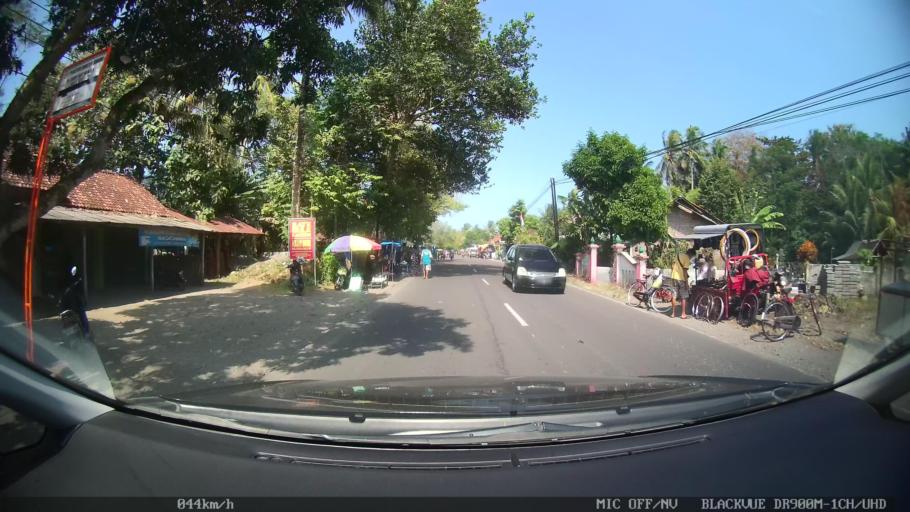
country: ID
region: Daerah Istimewa Yogyakarta
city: Srandakan
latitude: -7.9481
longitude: 110.2226
